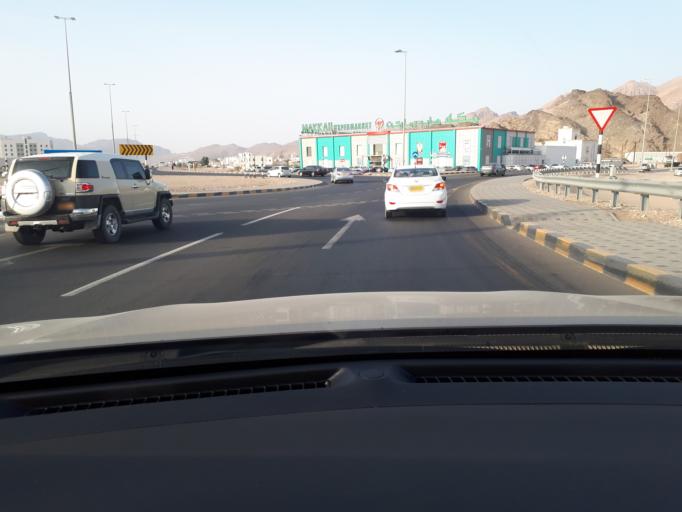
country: OM
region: Muhafazat Masqat
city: Bawshar
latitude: 23.4792
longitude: 58.4975
